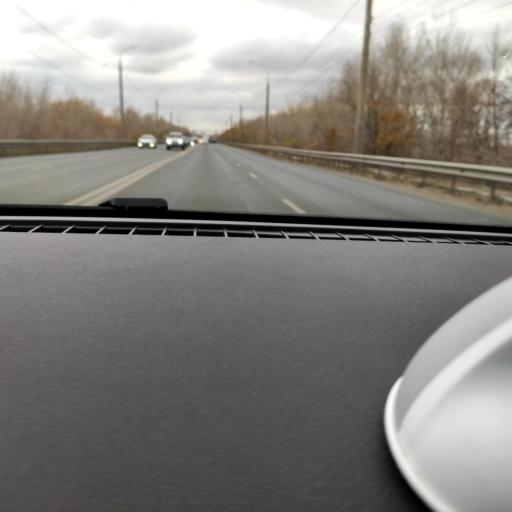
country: RU
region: Samara
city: Samara
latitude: 53.1465
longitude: 50.1833
